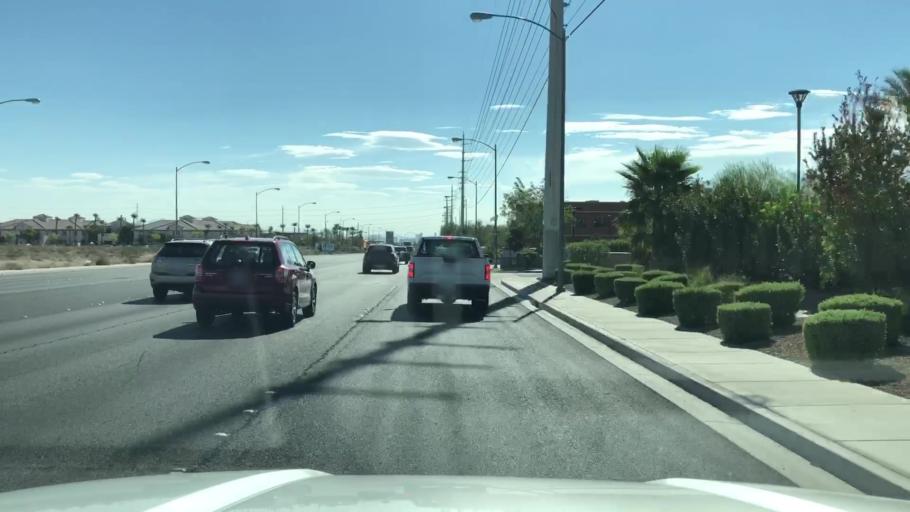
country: US
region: Nevada
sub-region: Clark County
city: Spring Valley
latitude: 36.1149
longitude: -115.2864
